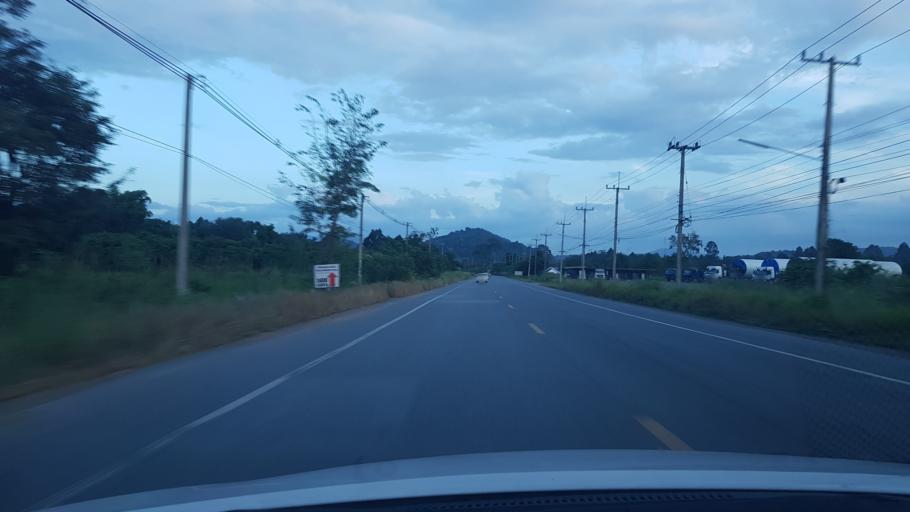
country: TH
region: Sara Buri
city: Kaeng Khoi
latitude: 14.4765
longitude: 101.0588
